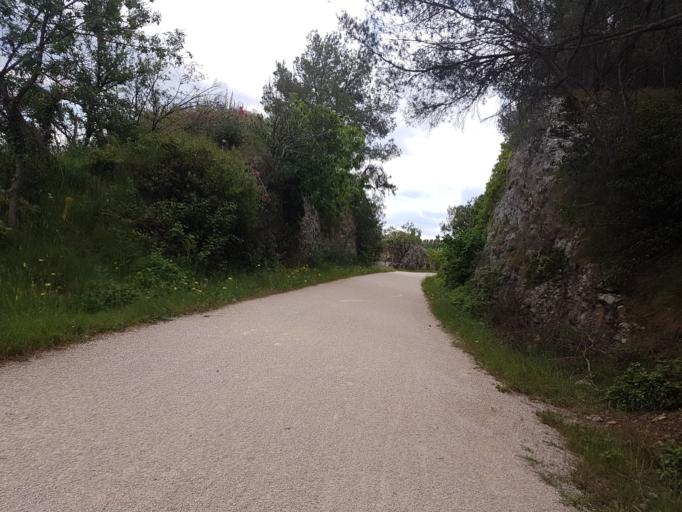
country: FR
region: Languedoc-Roussillon
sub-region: Departement du Gard
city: Vallabregues
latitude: 43.8267
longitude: 4.6247
